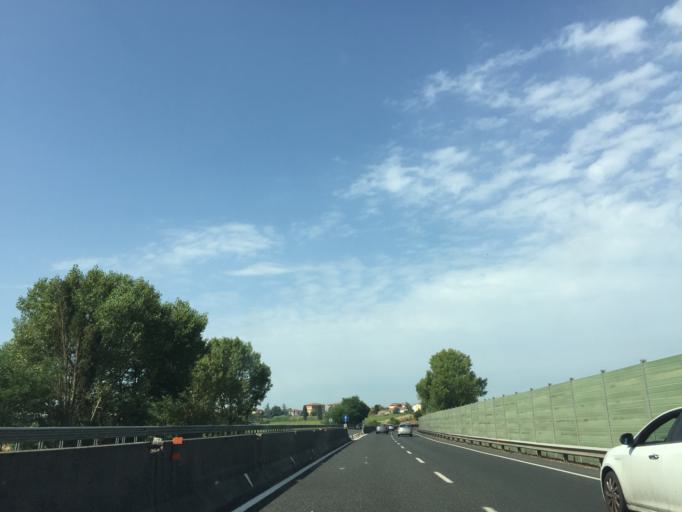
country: IT
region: Tuscany
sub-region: Province of Pisa
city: Il Romito
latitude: 43.6488
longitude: 10.6517
